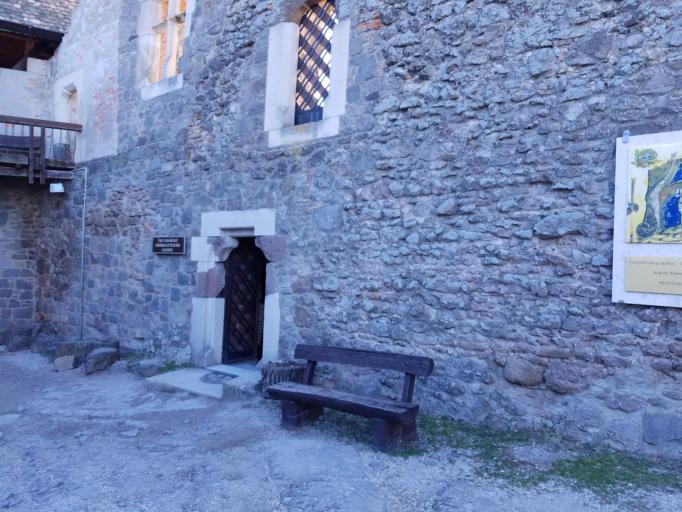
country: HU
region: Pest
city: Visegrad
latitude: 47.7936
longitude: 18.9804
